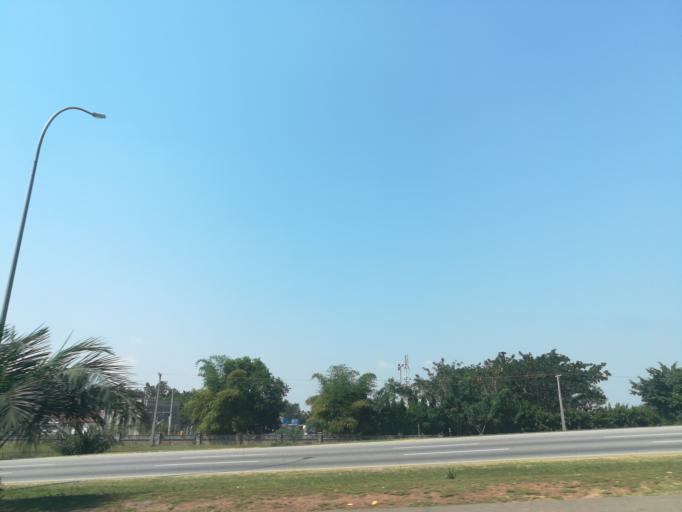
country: NG
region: Abuja Federal Capital Territory
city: Abuja
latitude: 9.0654
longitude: 7.4522
